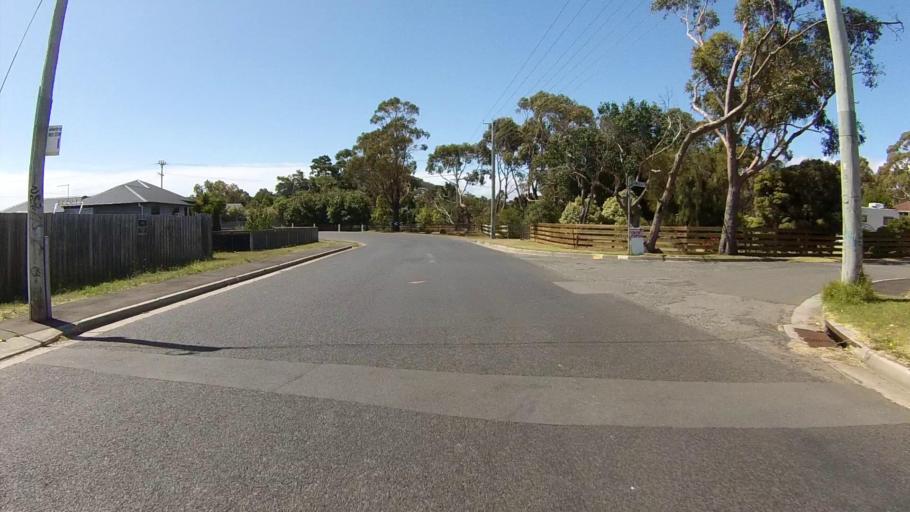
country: AU
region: Tasmania
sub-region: Clarence
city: Acton Park
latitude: -42.8945
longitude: 147.4975
